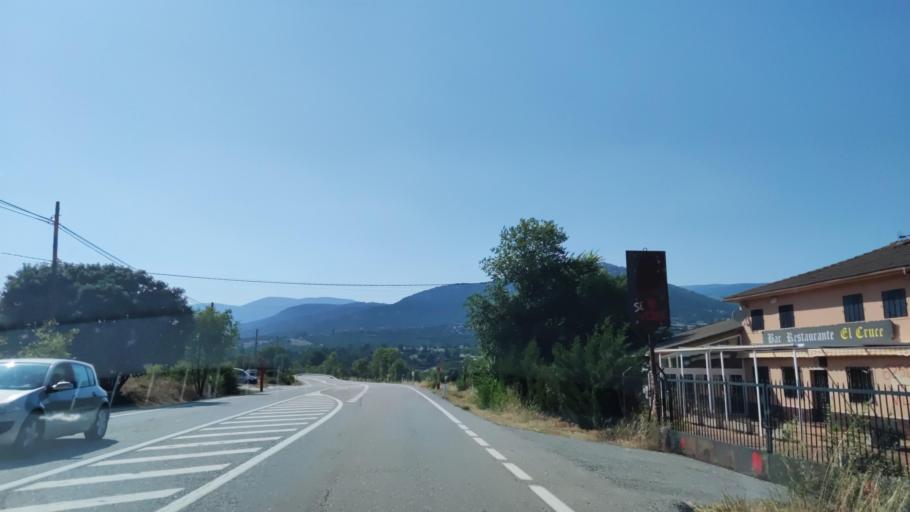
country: ES
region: Madrid
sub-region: Provincia de Madrid
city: Garganta de los Montes
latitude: 40.9429
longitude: -3.7092
